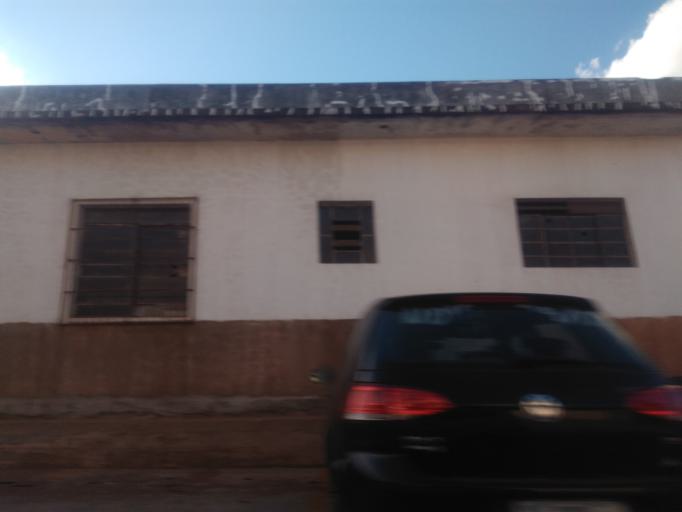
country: PY
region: Amambay
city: Pedro Juan Caballero
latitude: -22.5566
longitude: -55.7138
